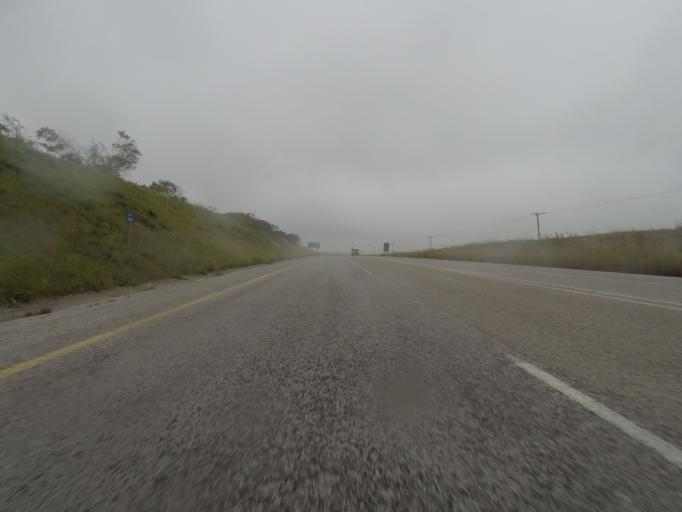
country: ZA
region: Eastern Cape
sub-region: Cacadu District Municipality
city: Grahamstown
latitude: -33.6255
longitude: 26.3022
